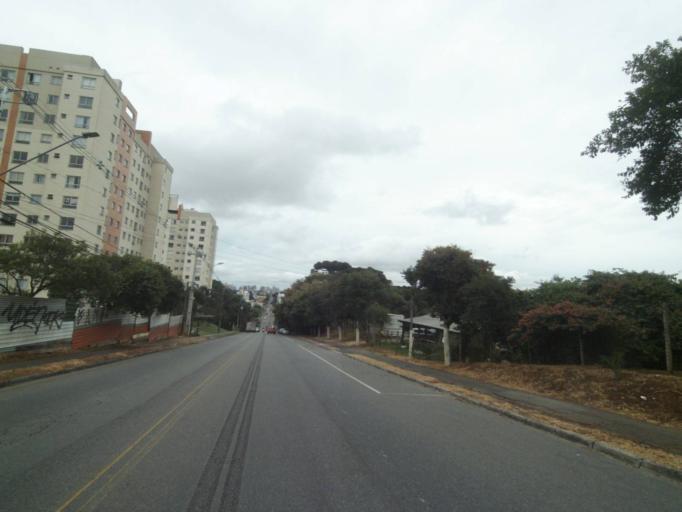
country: BR
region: Parana
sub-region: Curitiba
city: Curitiba
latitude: -25.4607
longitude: -49.3228
